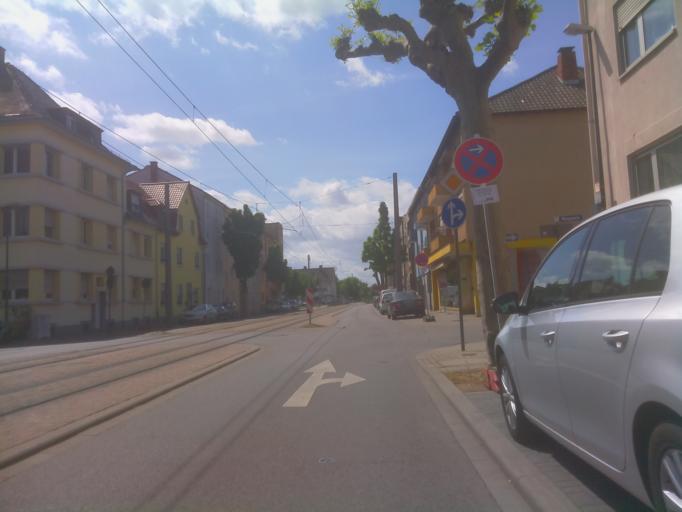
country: DE
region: Rheinland-Pfalz
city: Gartenstadt
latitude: 49.4588
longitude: 8.4273
